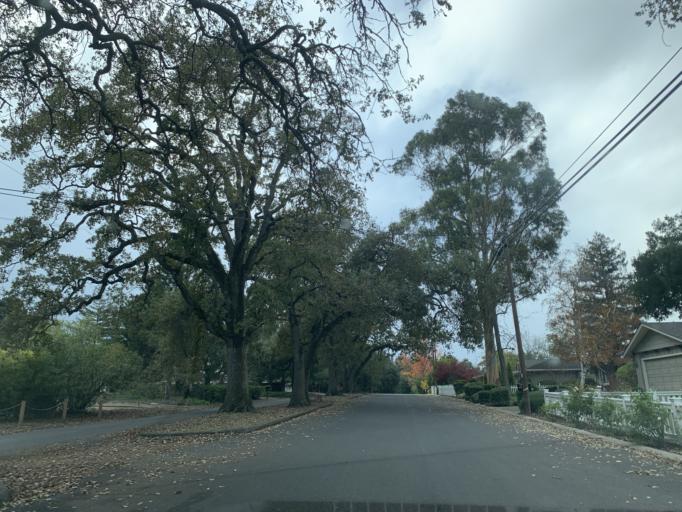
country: US
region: California
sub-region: Santa Clara County
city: Monte Sereno
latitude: 37.2507
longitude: -121.9929
